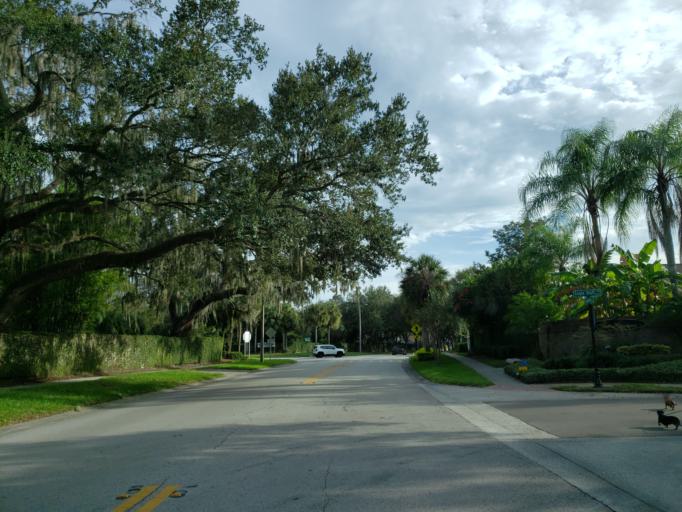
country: US
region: Florida
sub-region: Hillsborough County
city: Bloomingdale
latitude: 27.8830
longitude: -82.2447
